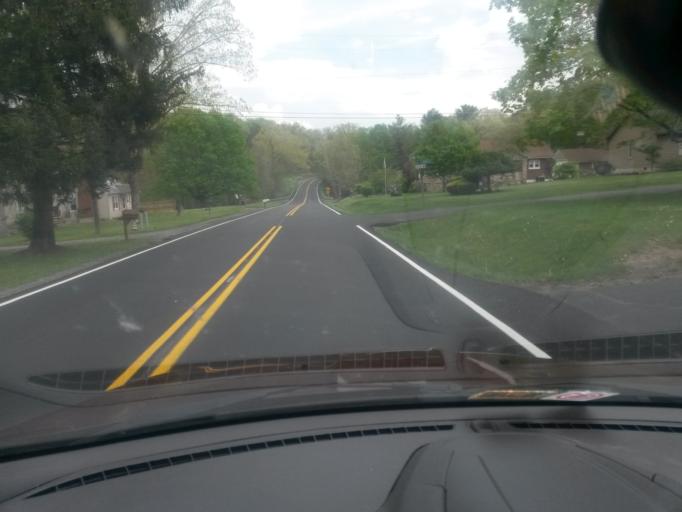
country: US
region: Virginia
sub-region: City of Covington
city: Covington
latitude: 37.8005
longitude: -80.0167
